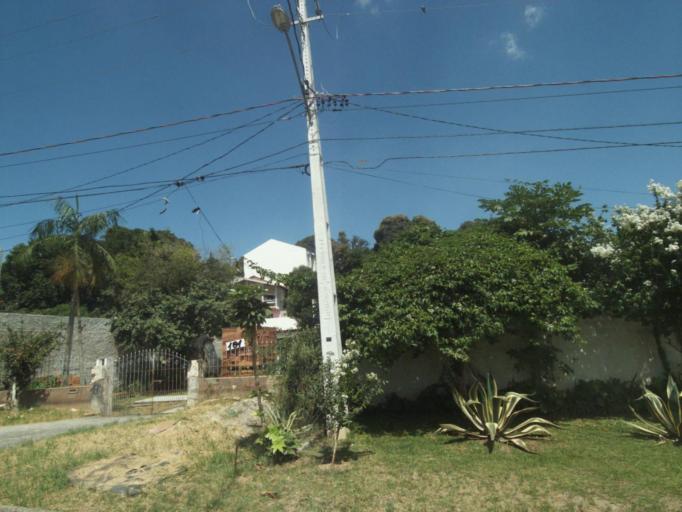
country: BR
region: Parana
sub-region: Curitiba
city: Curitiba
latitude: -25.4657
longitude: -49.2492
